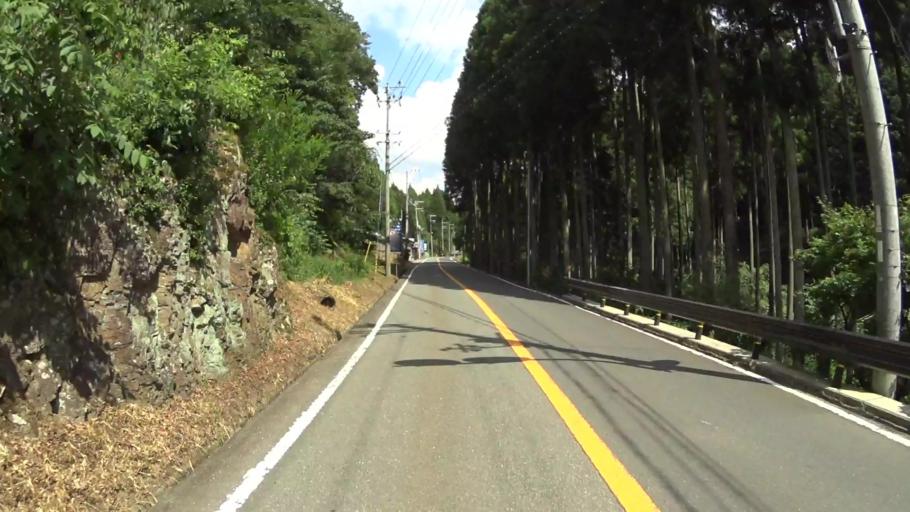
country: JP
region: Kyoto
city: Kameoka
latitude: 35.2775
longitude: 135.5567
